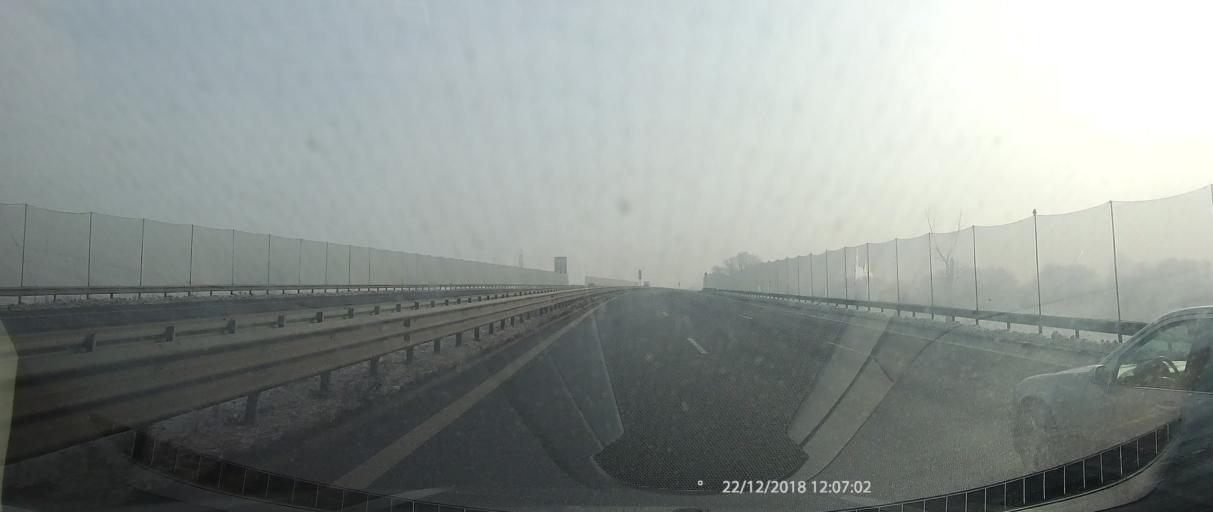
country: BG
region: Sofia-Capital
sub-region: Stolichna Obshtina
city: Sofia
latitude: 42.7499
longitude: 23.3560
